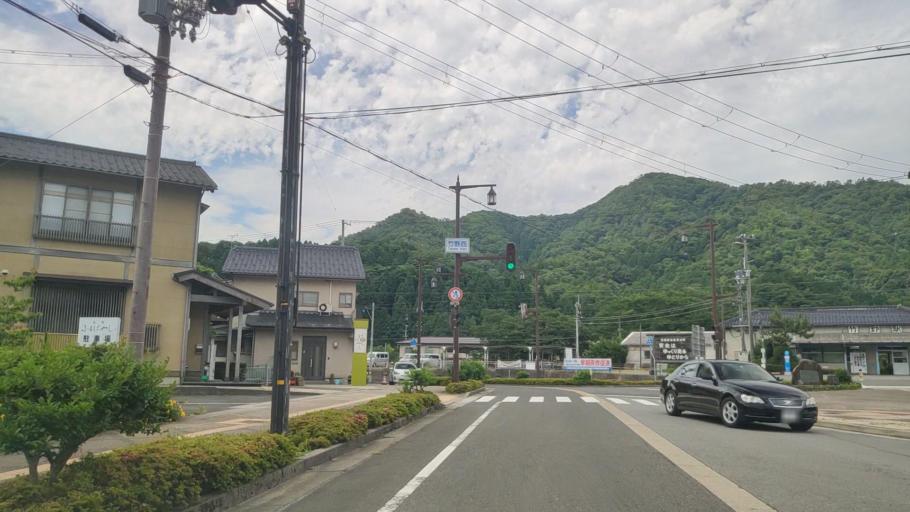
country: JP
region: Hyogo
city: Toyooka
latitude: 35.6504
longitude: 134.7571
